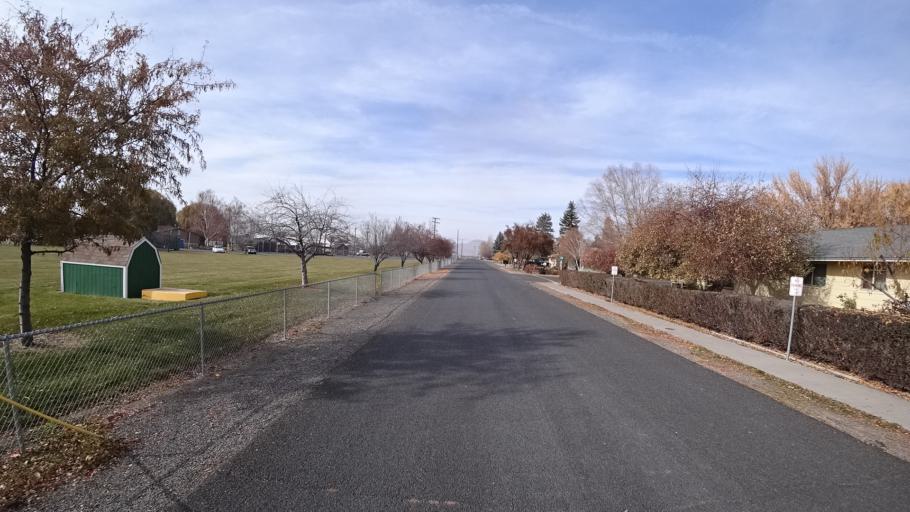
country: US
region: California
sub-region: Siskiyou County
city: Tulelake
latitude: 41.9510
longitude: -121.4774
